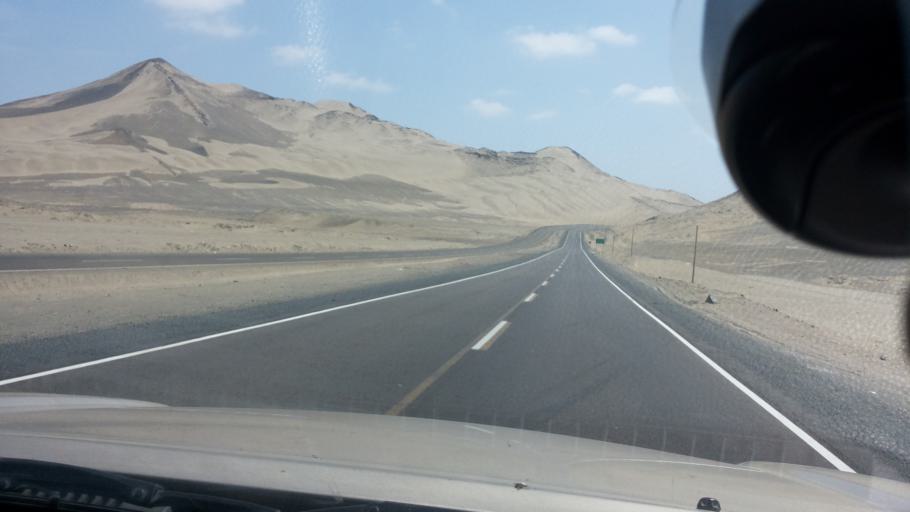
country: PE
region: Ancash
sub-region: Provincia de Casma
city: Casma
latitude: -9.6481
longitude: -78.2601
